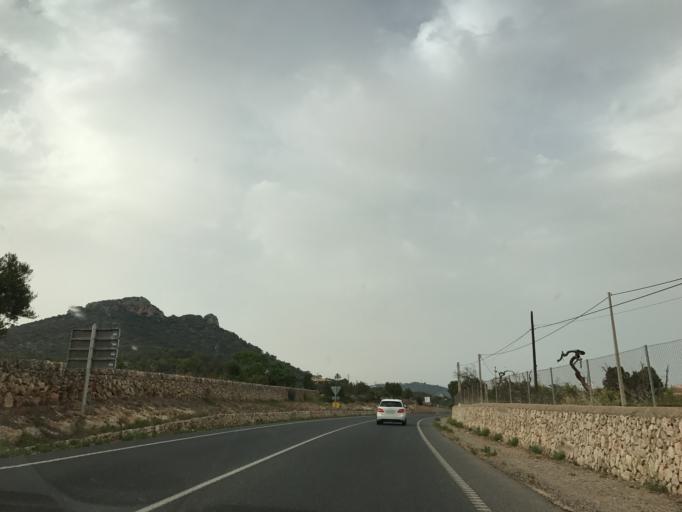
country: ES
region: Balearic Islands
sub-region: Illes Balears
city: Son Servera
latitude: 39.5962
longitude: 3.3664
